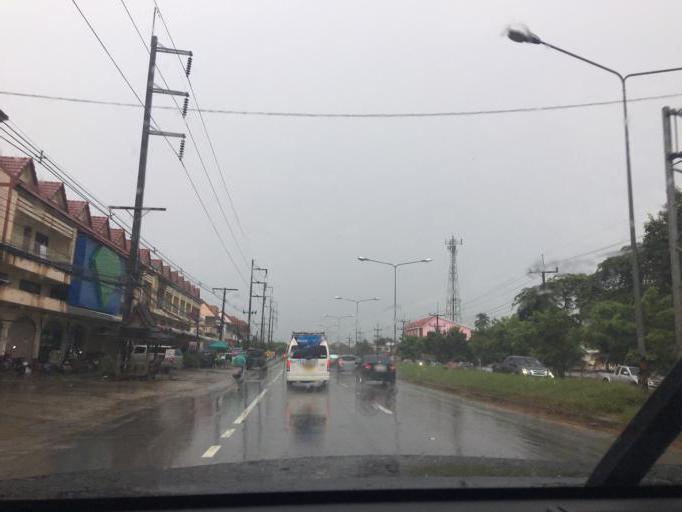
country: TH
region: Chiang Rai
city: Mae Fa Luang
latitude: 20.2639
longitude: 99.8576
